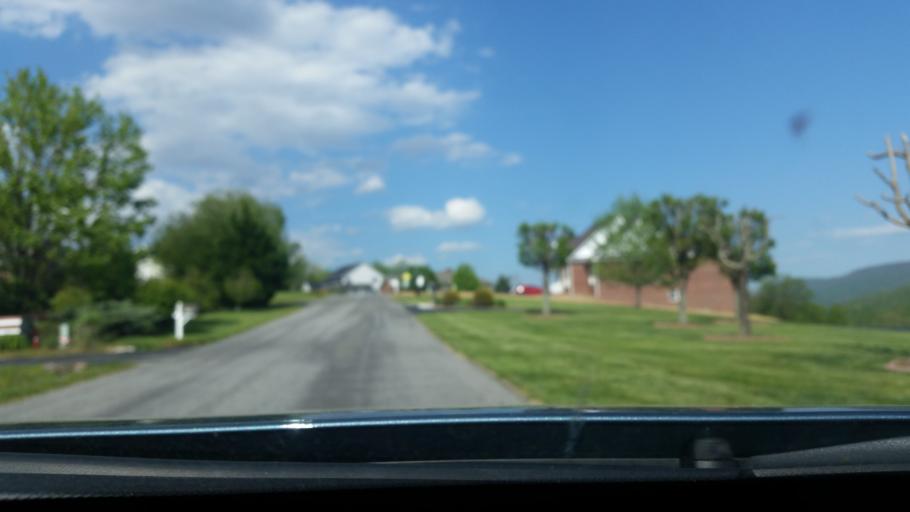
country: US
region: Virginia
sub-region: Giles County
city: Pembroke
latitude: 37.3067
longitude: -80.6344
